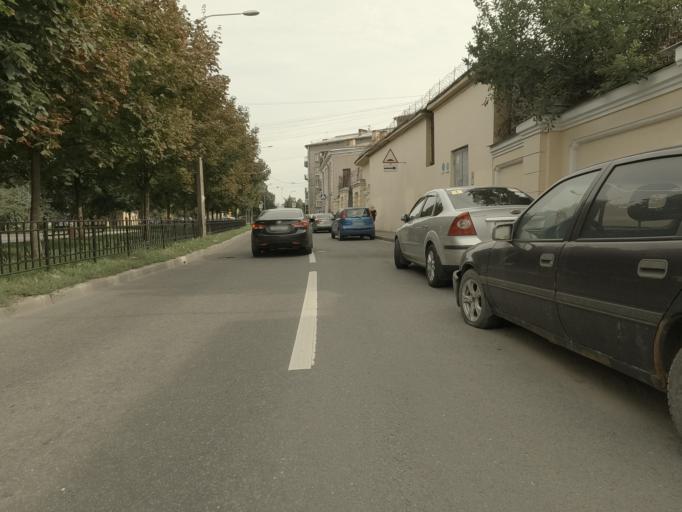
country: RU
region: St.-Petersburg
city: Admiralteisky
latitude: 59.9125
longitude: 30.2845
